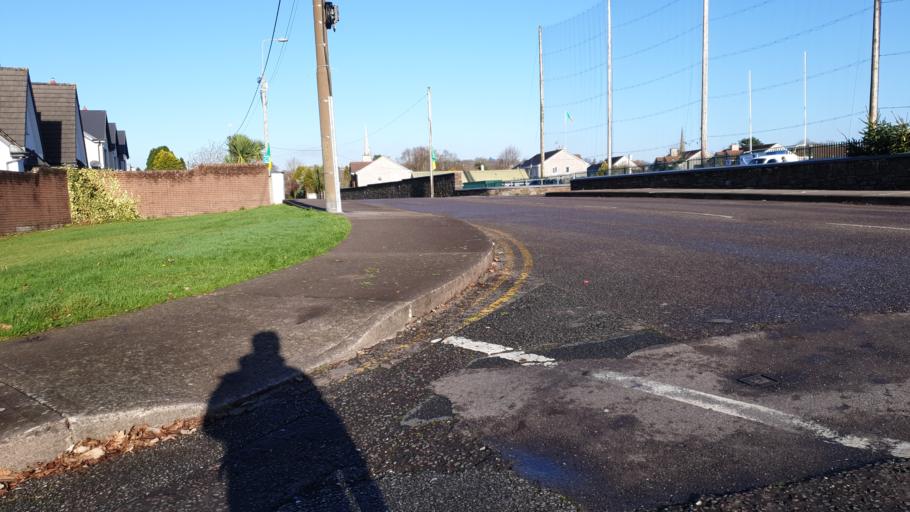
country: IE
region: Munster
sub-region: County Cork
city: Cork
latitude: 51.8926
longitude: -8.4197
